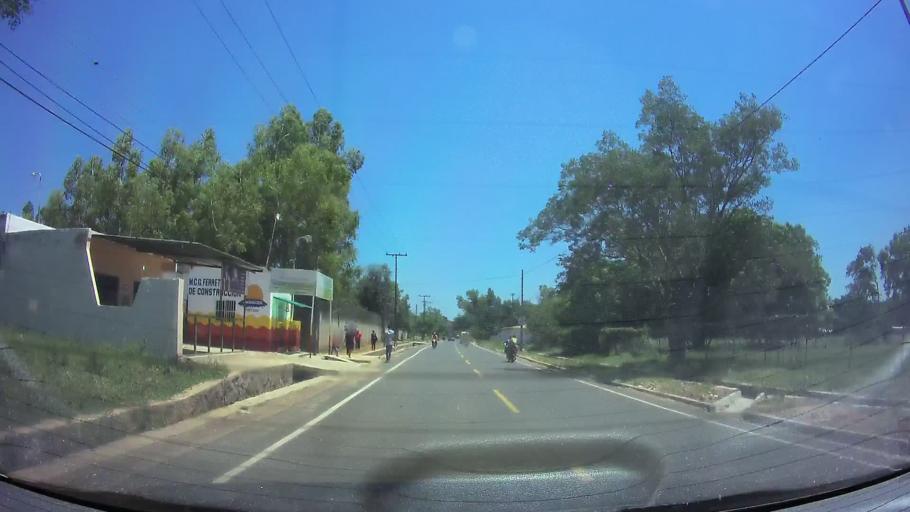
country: PY
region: Central
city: Limpio
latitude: -25.2471
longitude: -57.4910
